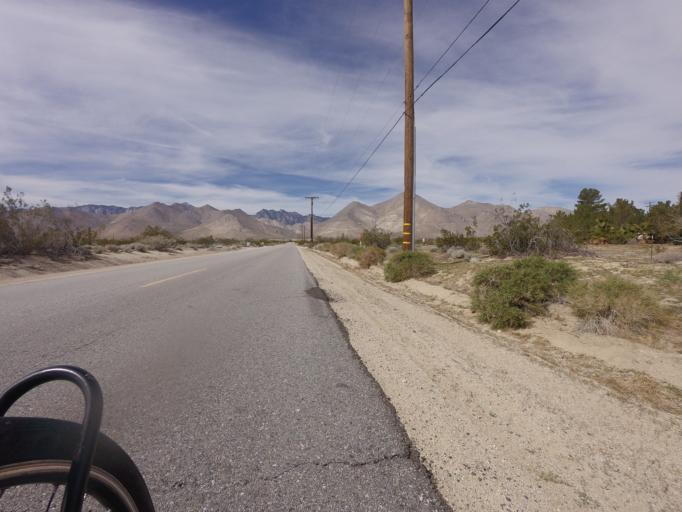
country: US
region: California
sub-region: Kern County
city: Inyokern
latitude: 35.7764
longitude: -117.8630
